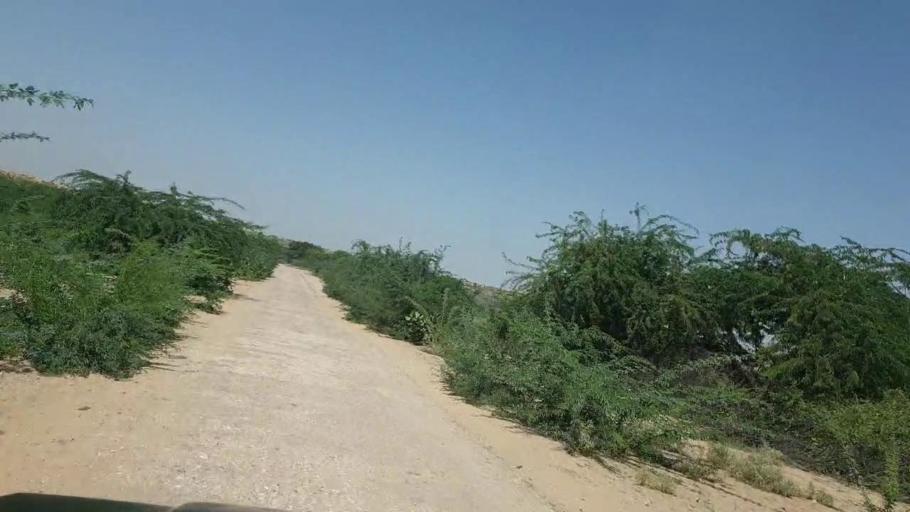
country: PK
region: Sindh
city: Chor
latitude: 25.4073
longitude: 70.3077
